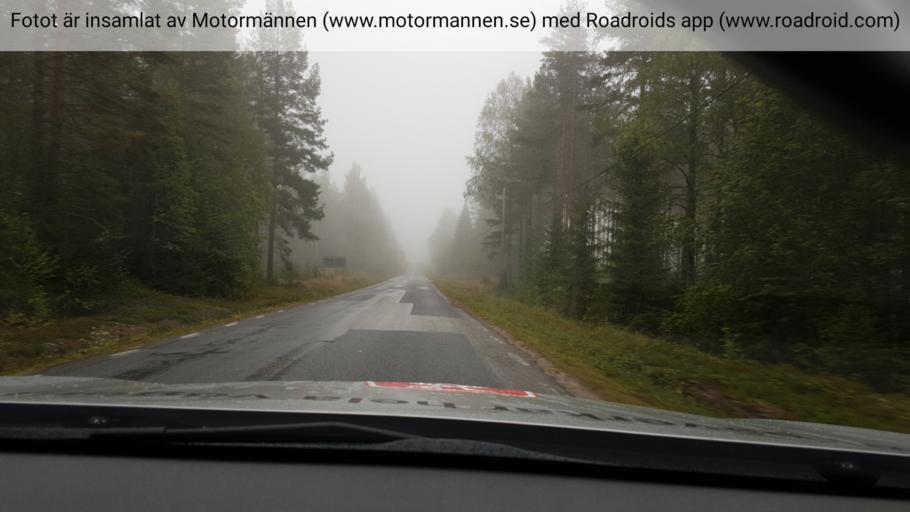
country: SE
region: Vaesterbotten
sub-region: Vannas Kommun
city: Vannasby
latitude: 64.0795
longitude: 20.0521
